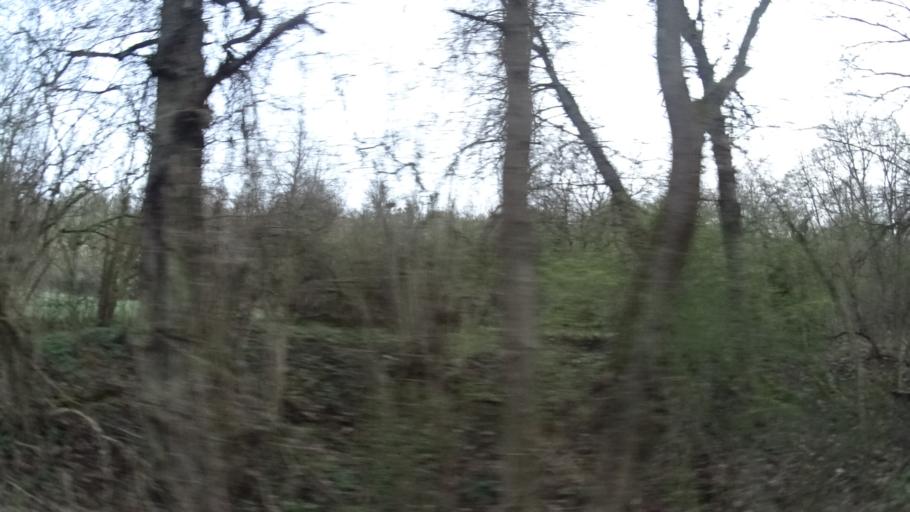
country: DE
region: Rheinland-Pfalz
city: Burgsponheim
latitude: 49.8304
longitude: 7.7082
